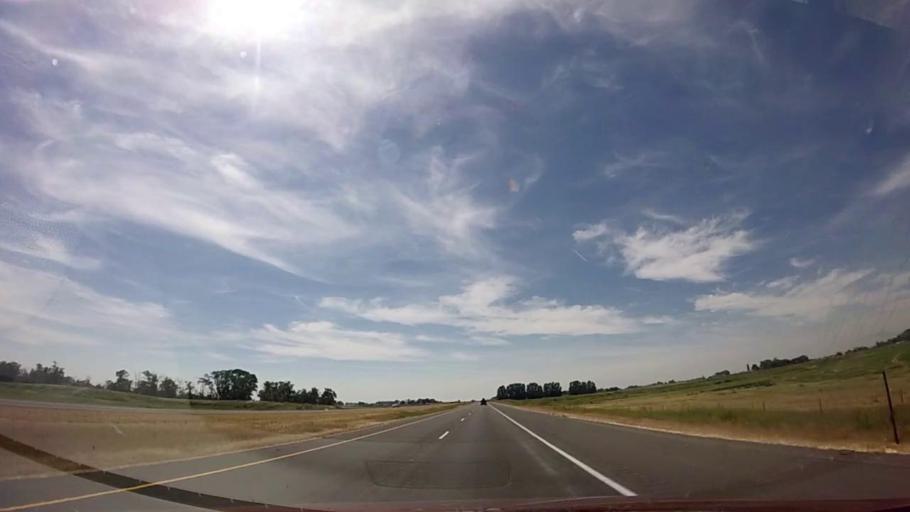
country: US
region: Idaho
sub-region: Minidoka County
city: Rupert
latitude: 42.5690
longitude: -113.6765
